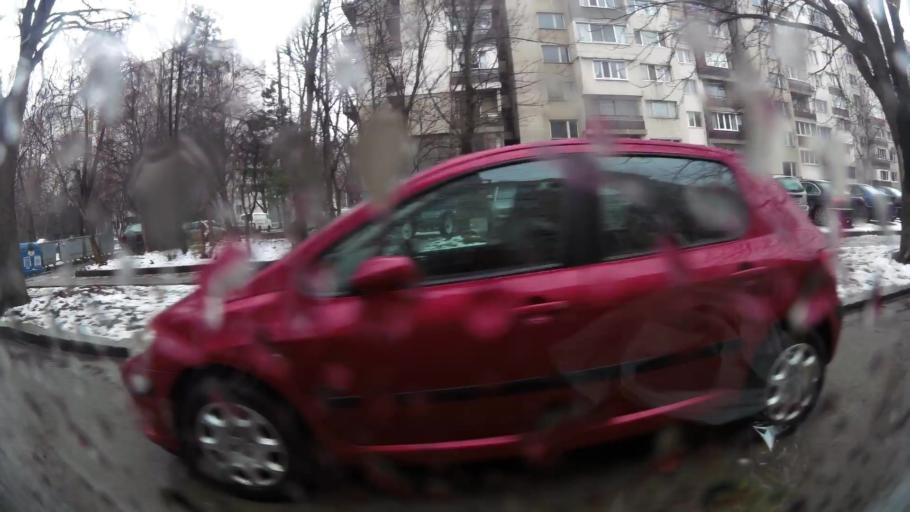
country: BG
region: Sofia-Capital
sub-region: Stolichna Obshtina
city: Sofia
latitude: 42.6727
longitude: 23.2989
